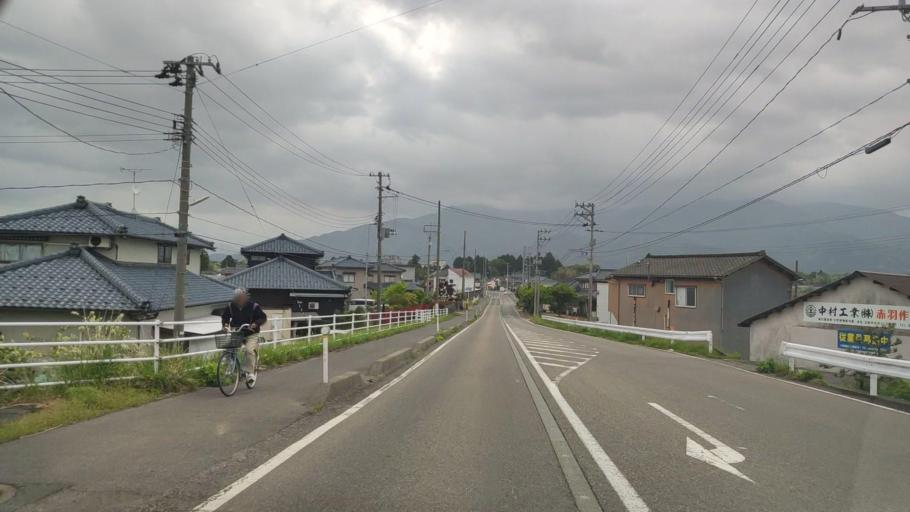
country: JP
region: Niigata
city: Gosen
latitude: 37.7323
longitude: 139.2046
